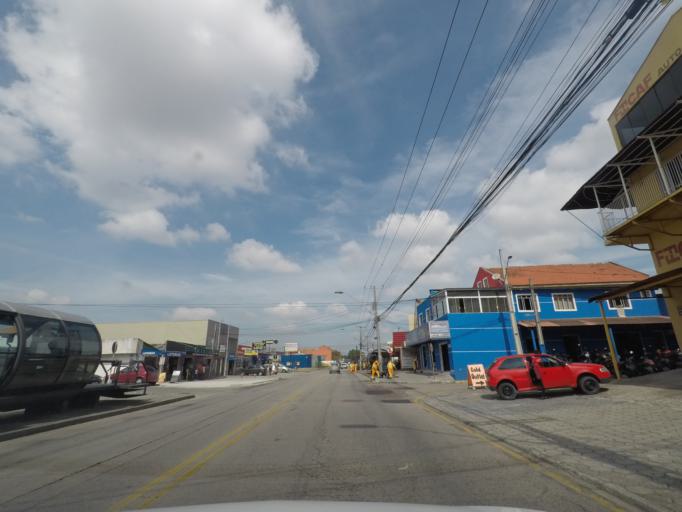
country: BR
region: Parana
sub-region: Pinhais
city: Pinhais
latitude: -25.4650
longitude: -49.2099
